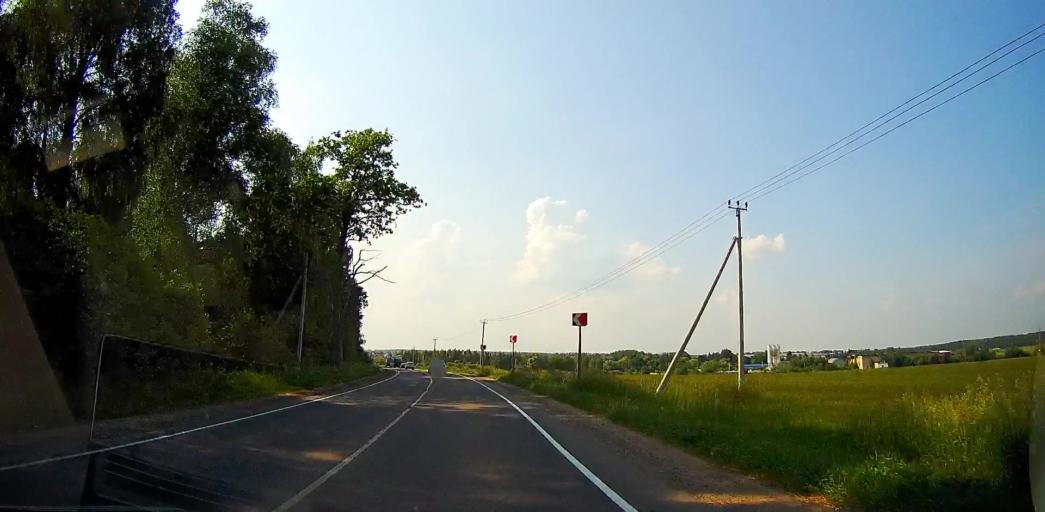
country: RU
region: Moskovskaya
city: Zhitnevo
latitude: 55.3082
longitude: 37.9088
